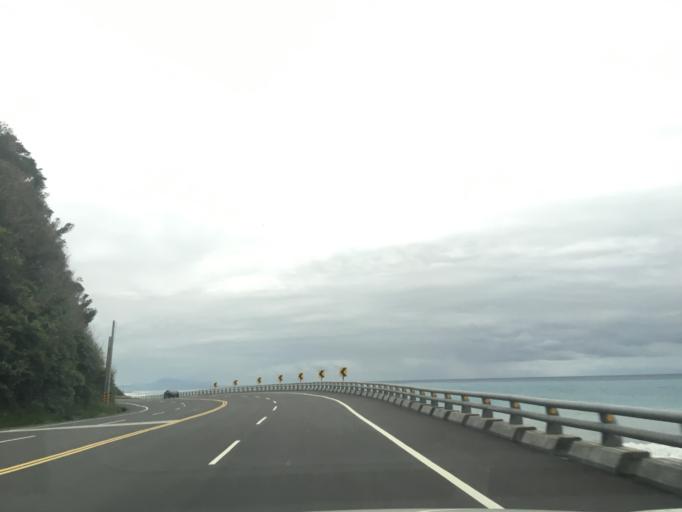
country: TW
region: Taiwan
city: Taitung City
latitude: 22.4343
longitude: 120.9357
